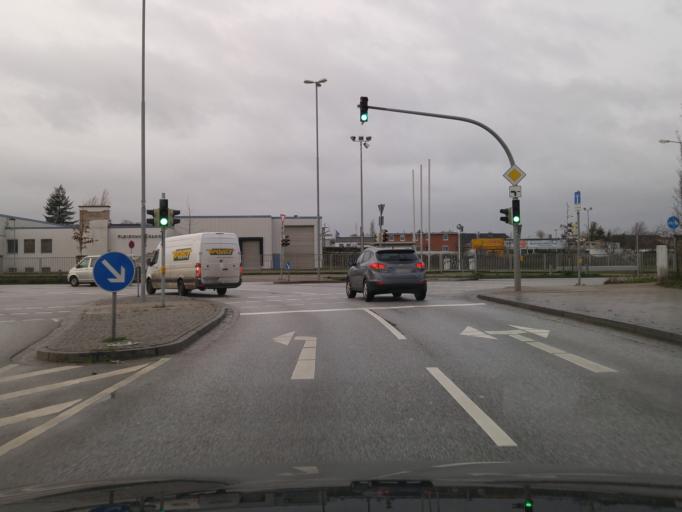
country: DE
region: Schleswig-Holstein
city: Luebeck
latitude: 53.8843
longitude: 10.6912
